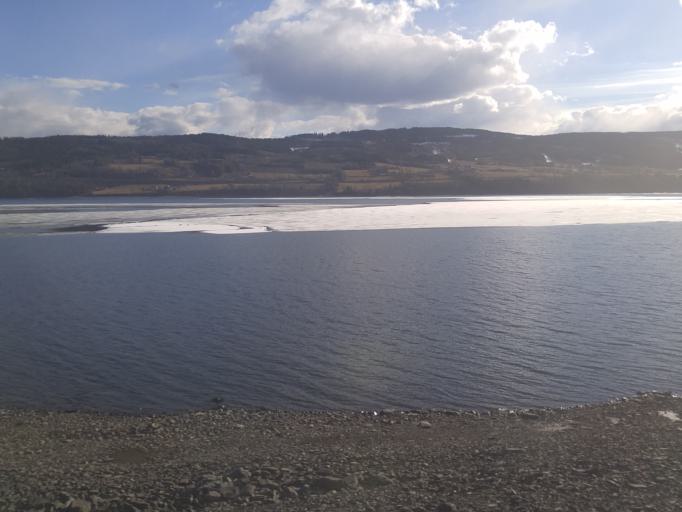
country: NO
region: Hedmark
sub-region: Ringsaker
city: Moelv
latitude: 61.0009
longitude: 10.5800
